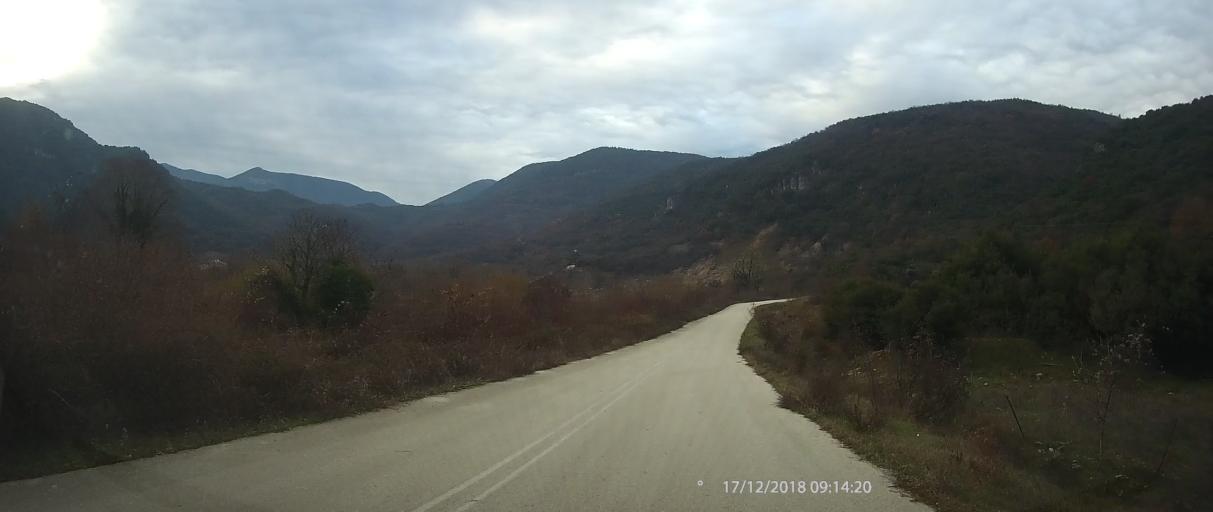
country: GR
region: Epirus
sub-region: Nomos Ioanninon
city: Kalpaki
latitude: 39.9743
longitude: 20.6564
